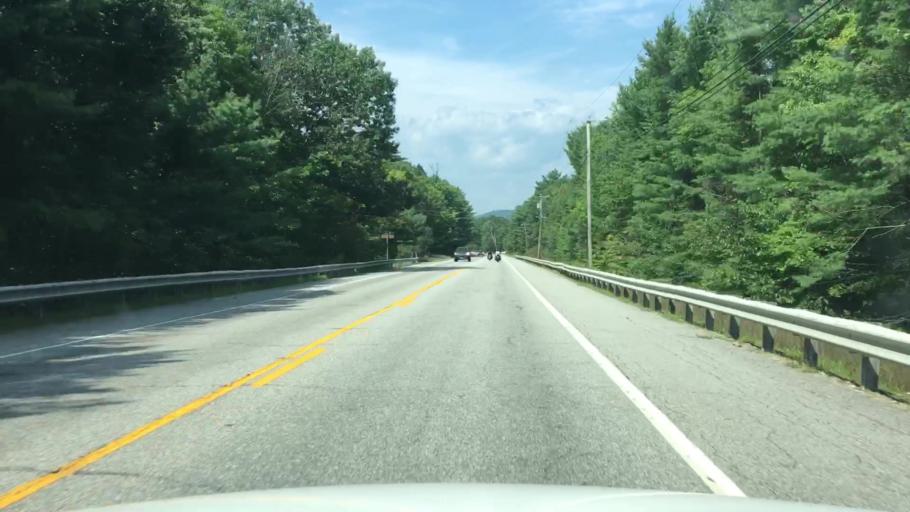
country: US
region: Maine
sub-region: Oxford County
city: Peru
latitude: 44.4916
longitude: -70.3840
